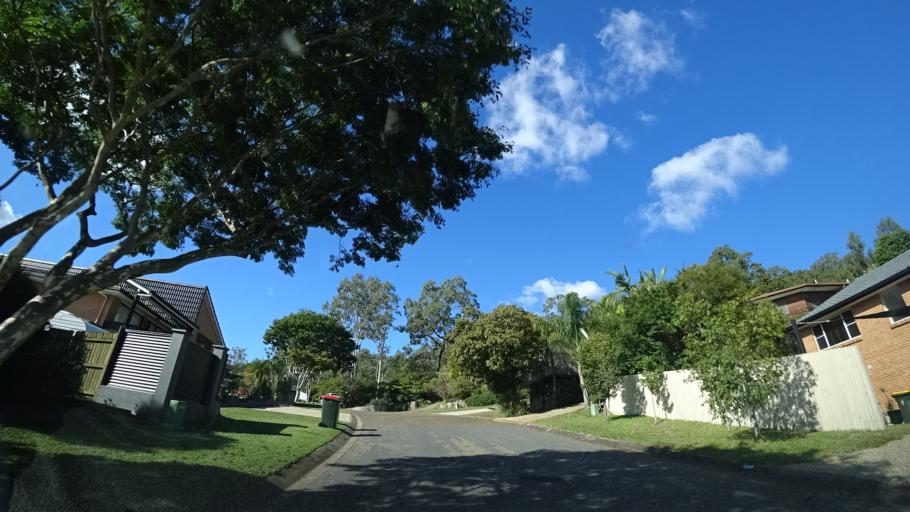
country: AU
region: Queensland
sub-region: Brisbane
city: Taringa
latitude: -27.4535
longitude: 152.9571
